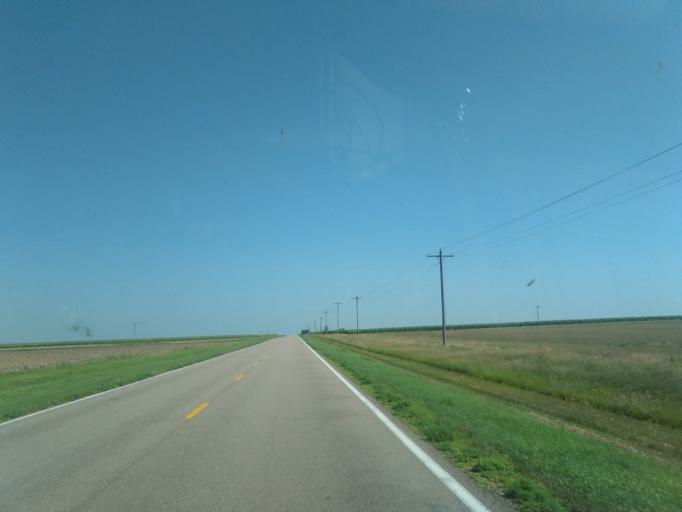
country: US
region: Kansas
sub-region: Cheyenne County
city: Saint Francis
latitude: 39.7836
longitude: -101.5420
